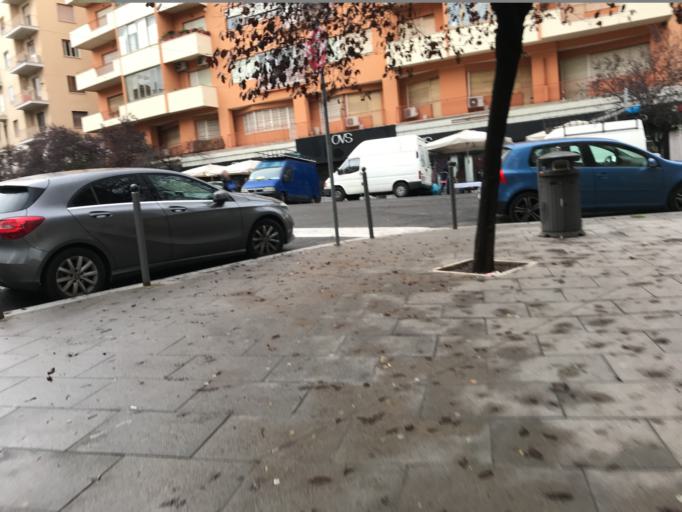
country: IT
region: Latium
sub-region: Citta metropolitana di Roma Capitale
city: Rome
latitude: 41.9130
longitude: 12.5179
